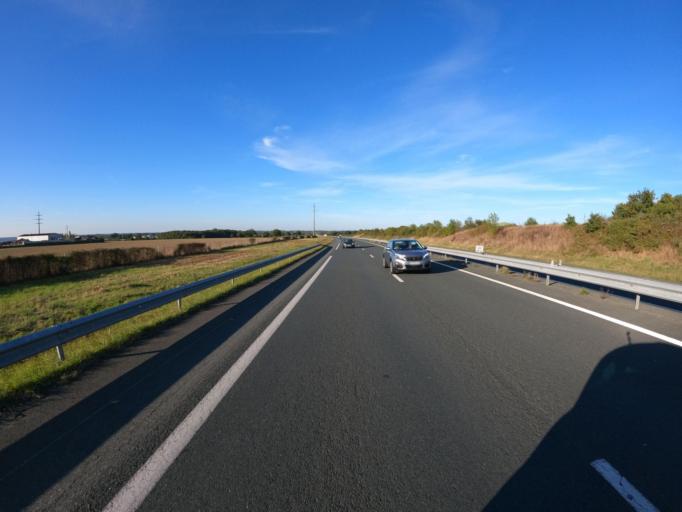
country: FR
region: Pays de la Loire
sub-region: Departement de Maine-et-Loire
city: Mazieres-en-Mauges
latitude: 47.0651
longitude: -0.8272
